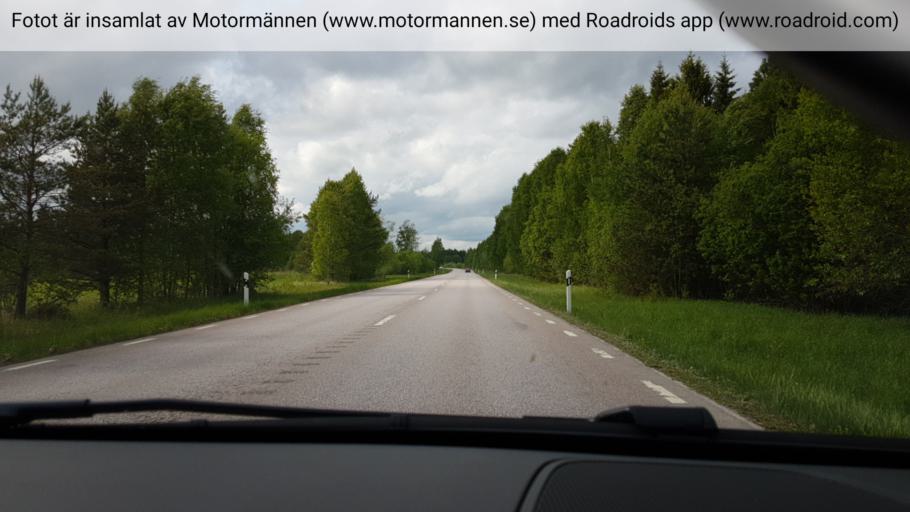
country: SE
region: Uppsala
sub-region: Tierps Kommun
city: Orbyhus
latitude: 60.2501
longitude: 17.6459
